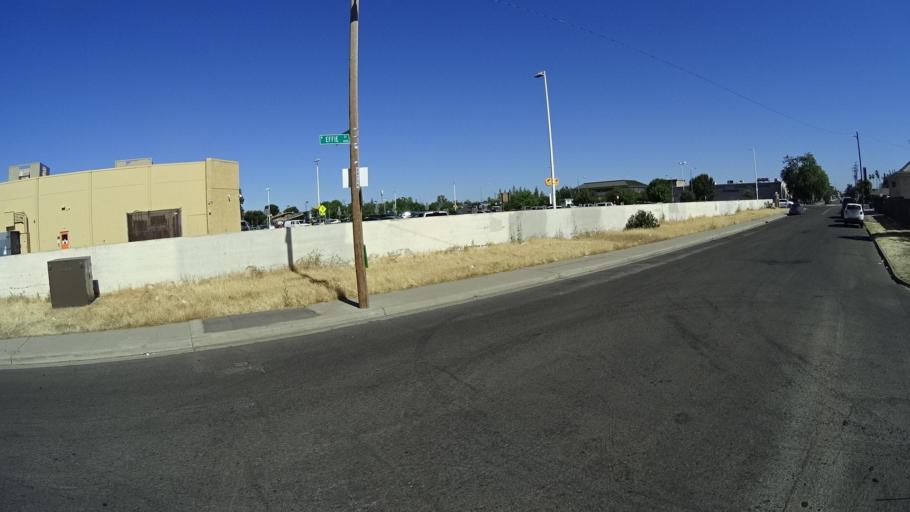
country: US
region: California
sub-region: Fresno County
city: Fresno
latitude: 36.7932
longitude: -119.7882
